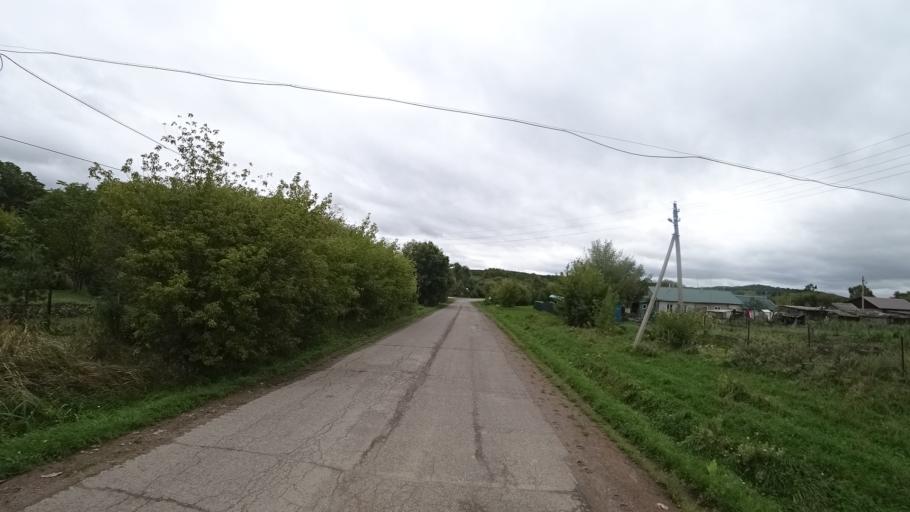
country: RU
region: Primorskiy
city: Chernigovka
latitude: 44.4623
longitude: 132.5912
